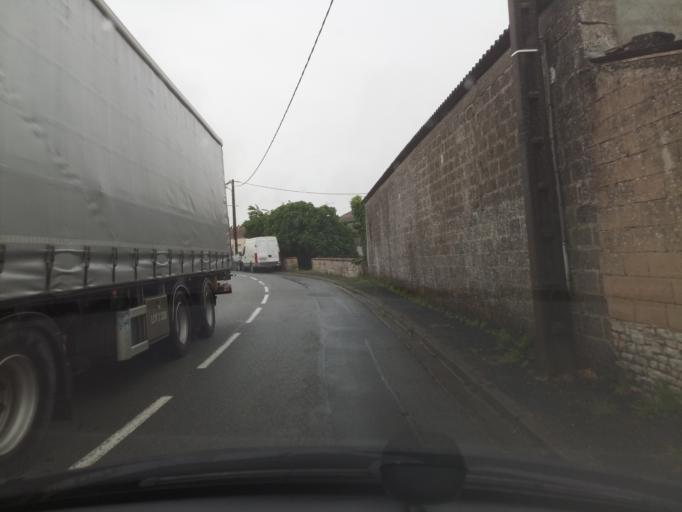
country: FR
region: Poitou-Charentes
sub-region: Departement de la Charente-Maritime
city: Andilly
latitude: 46.2316
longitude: -0.9957
